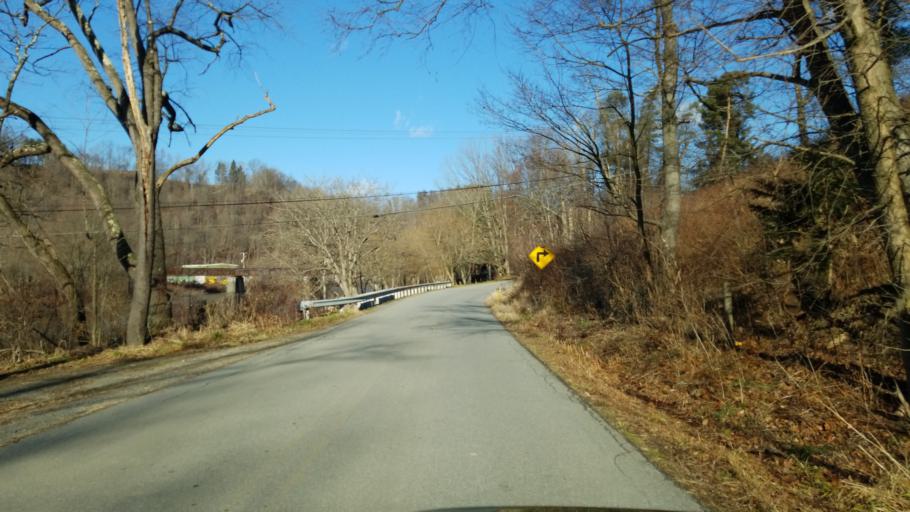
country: US
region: Pennsylvania
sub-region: Clearfield County
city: Curwensville
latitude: 40.9791
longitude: -78.4936
